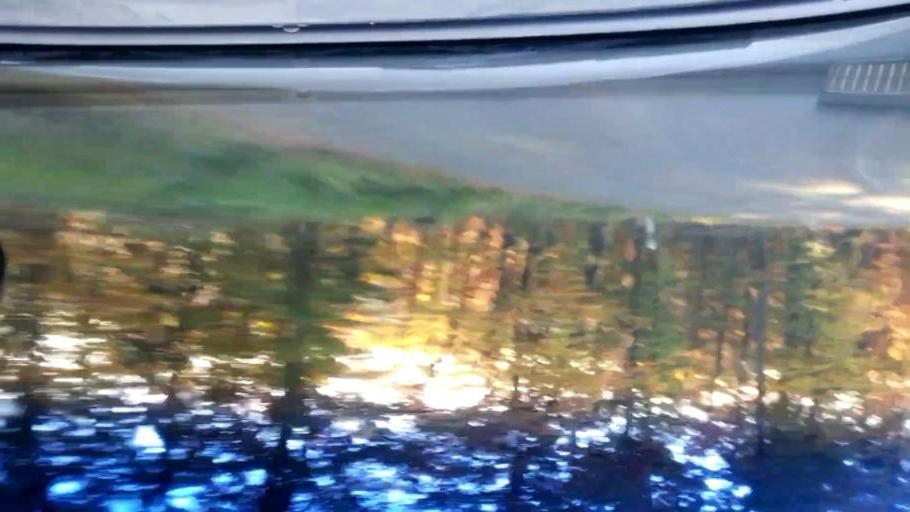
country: DE
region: Bavaria
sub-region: Upper Franconia
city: Unterleinleiter
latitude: 49.8387
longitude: 11.1994
